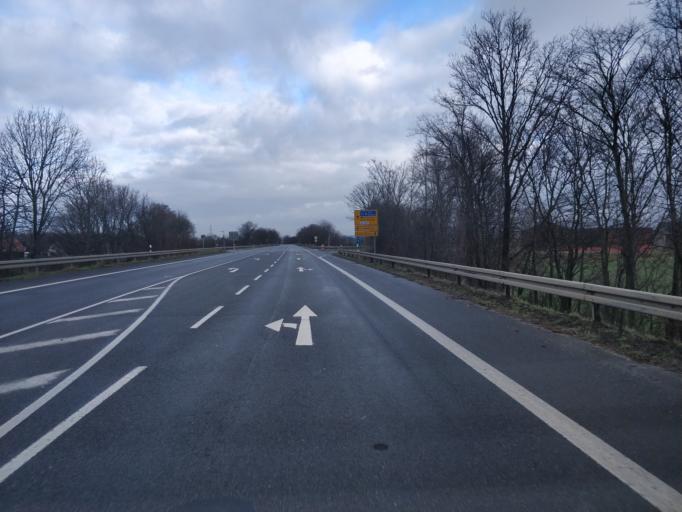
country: DE
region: North Rhine-Westphalia
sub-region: Regierungsbezirk Koln
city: Euskirchen
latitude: 50.6573
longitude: 6.8446
